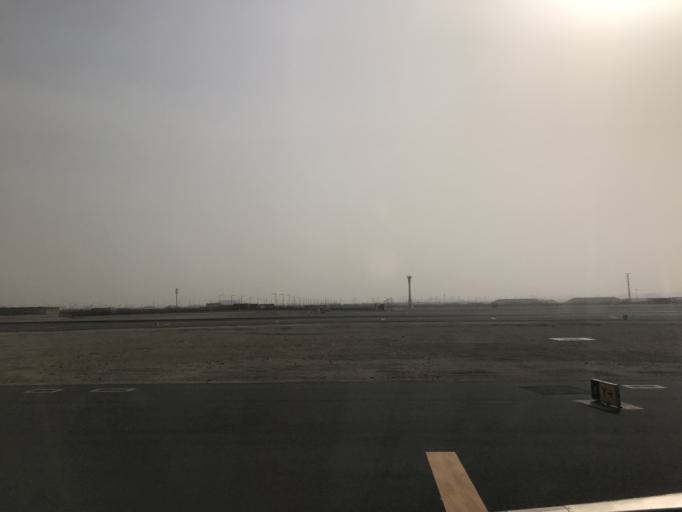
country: QA
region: Baladiyat ad Dawhah
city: Doha
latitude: 25.2790
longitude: 51.5971
